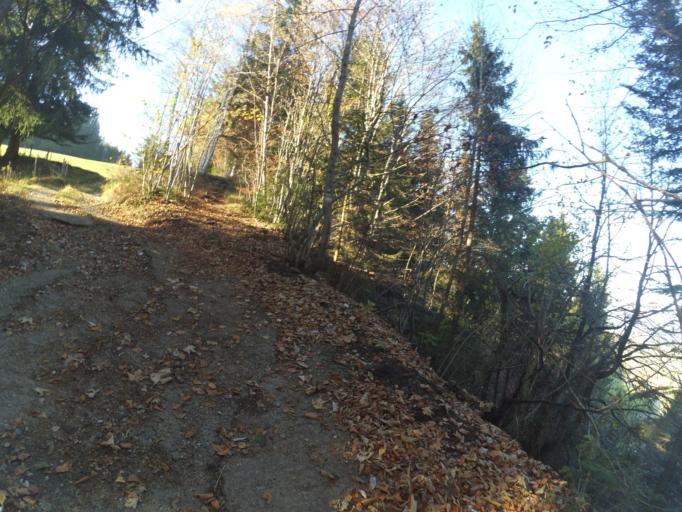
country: DE
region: Bavaria
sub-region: Upper Bavaria
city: Bernbeuren
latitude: 47.7329
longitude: 10.7428
